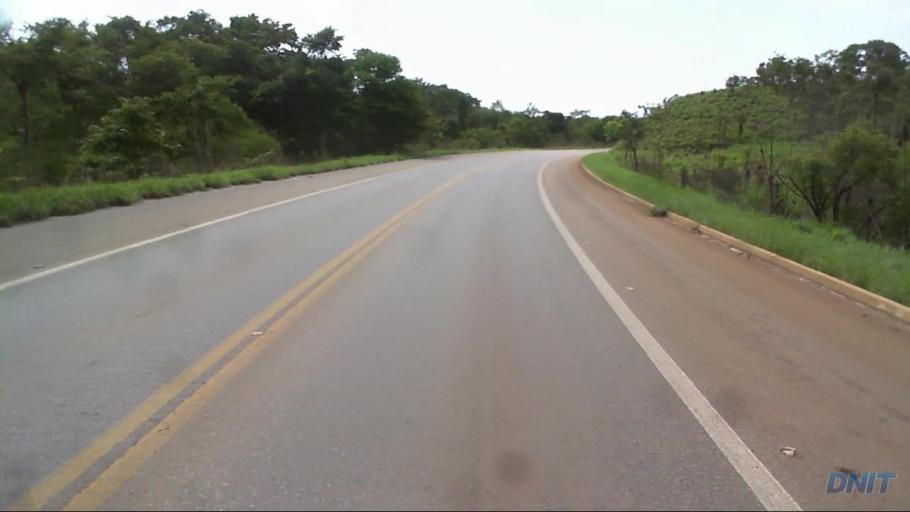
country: BR
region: Goias
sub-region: Barro Alto
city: Barro Alto
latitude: -15.1569
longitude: -48.8025
